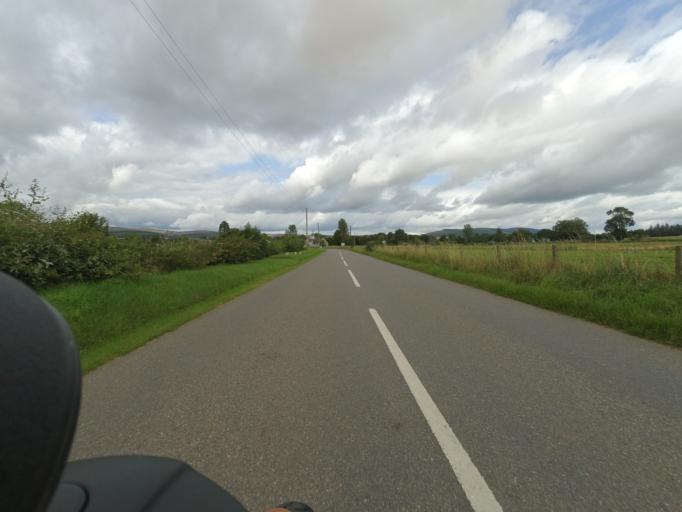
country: GB
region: Scotland
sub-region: Aberdeenshire
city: Laurencekirk
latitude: 56.8440
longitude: -2.5673
